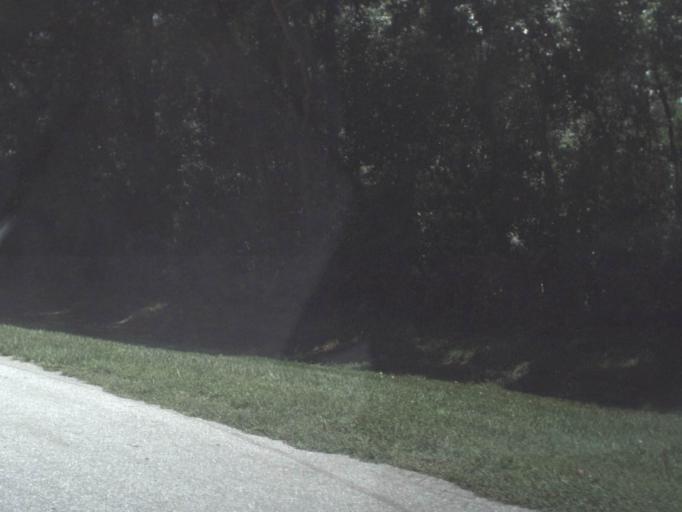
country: US
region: Florida
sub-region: Duval County
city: Jacksonville
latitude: 30.2931
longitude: -81.5923
